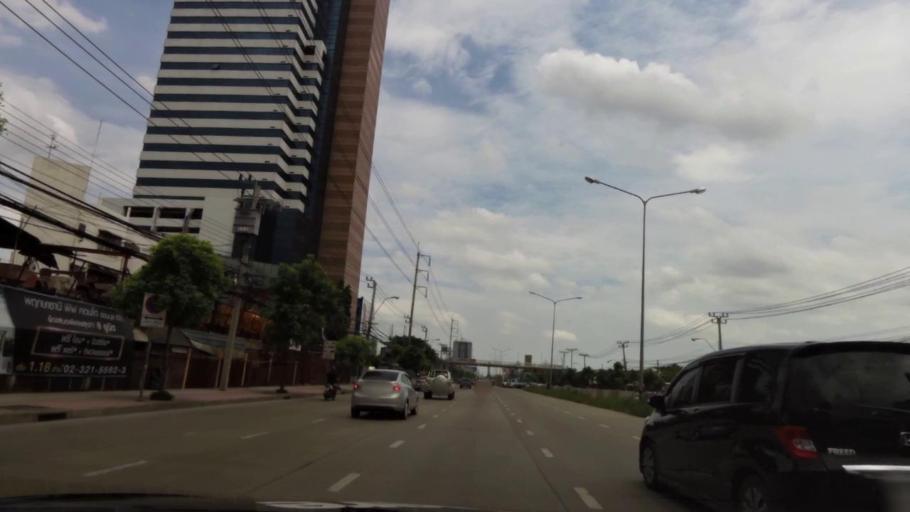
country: TH
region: Bangkok
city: Suan Luang
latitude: 13.7313
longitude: 100.6414
